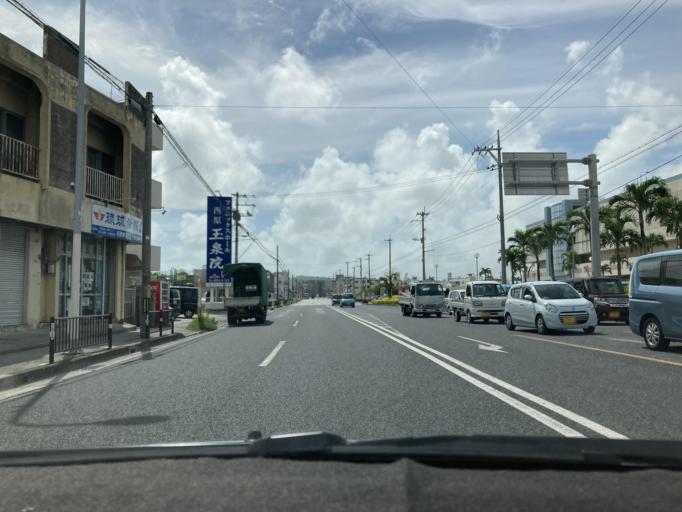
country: JP
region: Okinawa
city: Ginowan
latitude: 26.2250
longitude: 127.7661
